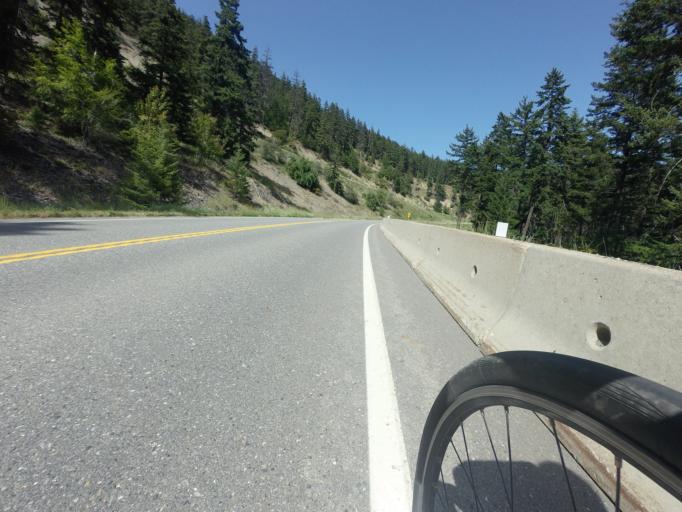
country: CA
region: British Columbia
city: Lillooet
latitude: 50.6540
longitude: -122.0103
